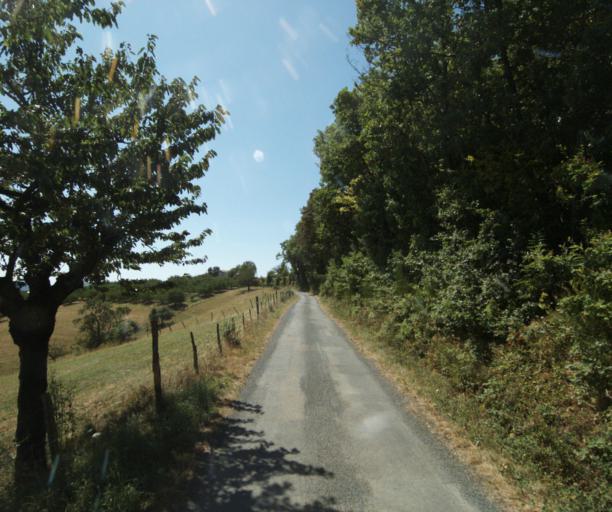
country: FR
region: Rhone-Alpes
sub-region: Departement du Rhone
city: Bessenay
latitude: 45.7831
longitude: 4.5246
